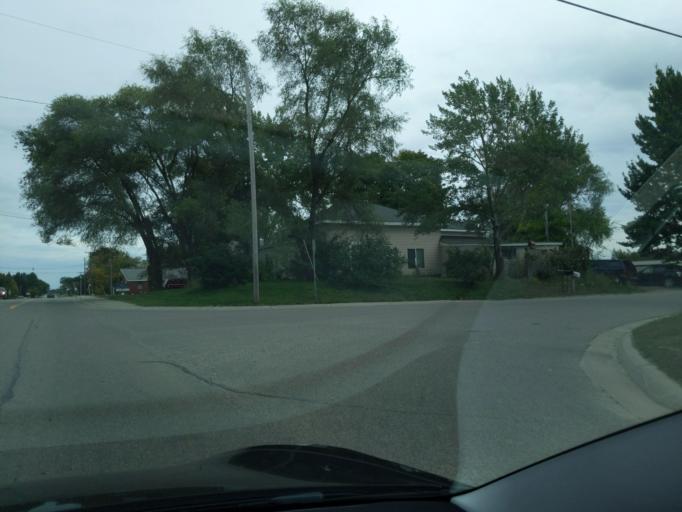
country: US
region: Michigan
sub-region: Clare County
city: Clare
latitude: 43.8346
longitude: -84.8625
